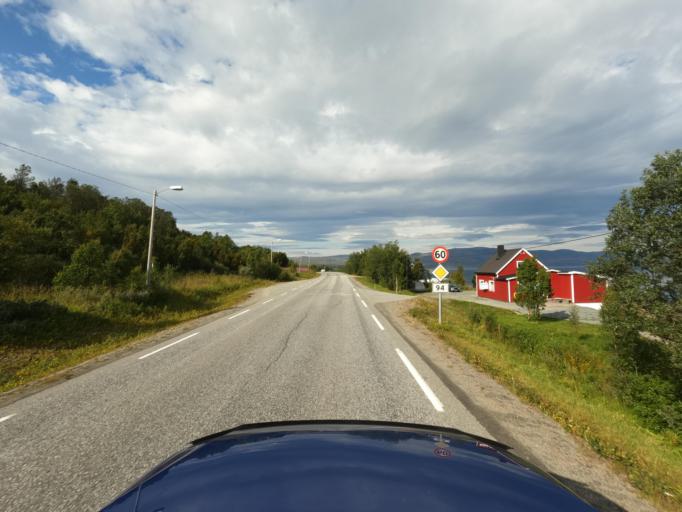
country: NO
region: Finnmark Fylke
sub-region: Kvalsund
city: Kvalsund
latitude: 70.4961
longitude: 24.0894
